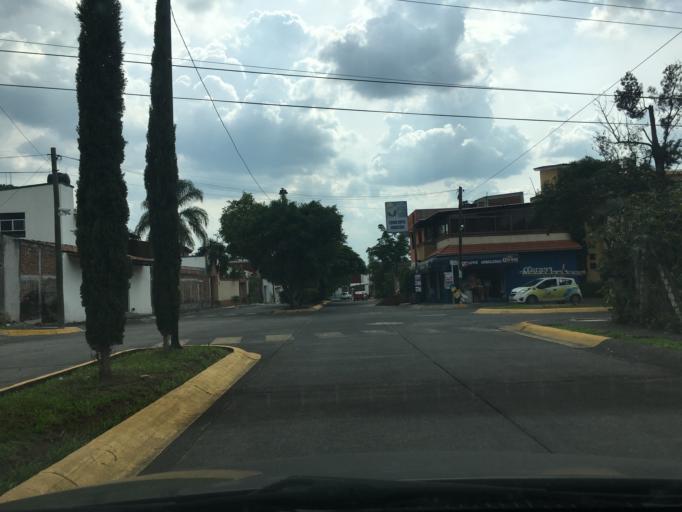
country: MX
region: Michoacan
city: Morelia
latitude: 19.6801
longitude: -101.2083
